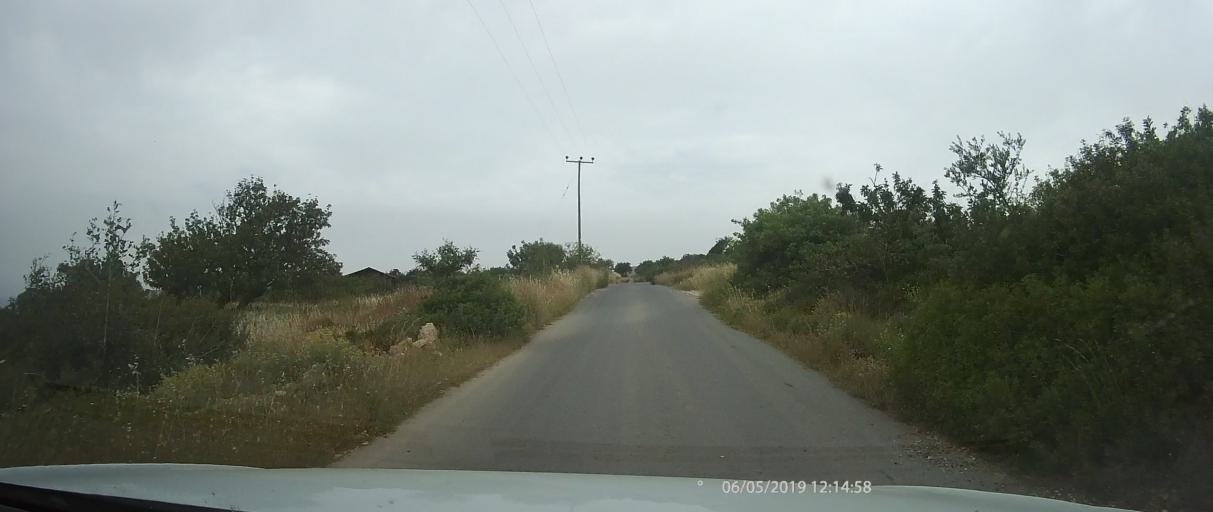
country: CY
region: Pafos
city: Tala
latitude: 34.8491
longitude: 32.4224
